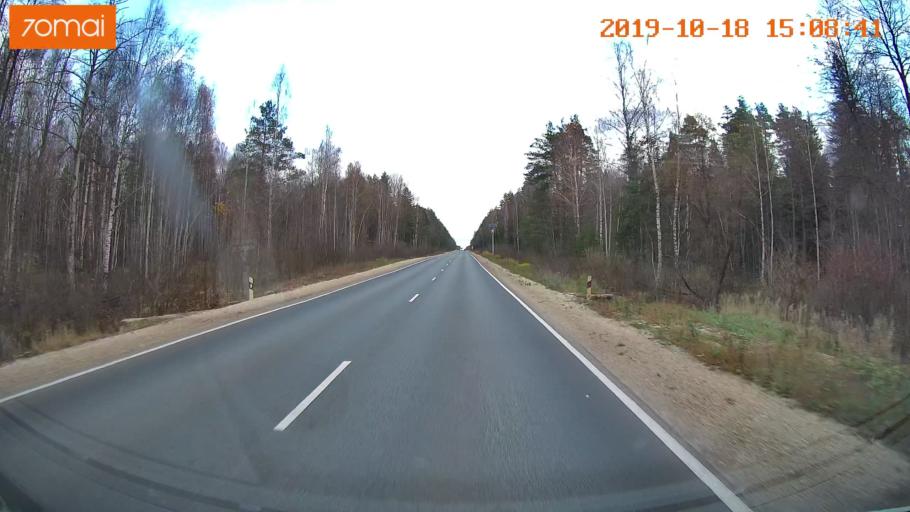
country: RU
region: Vladimir
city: Gus'-Khrustal'nyy
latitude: 55.5557
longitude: 40.6131
